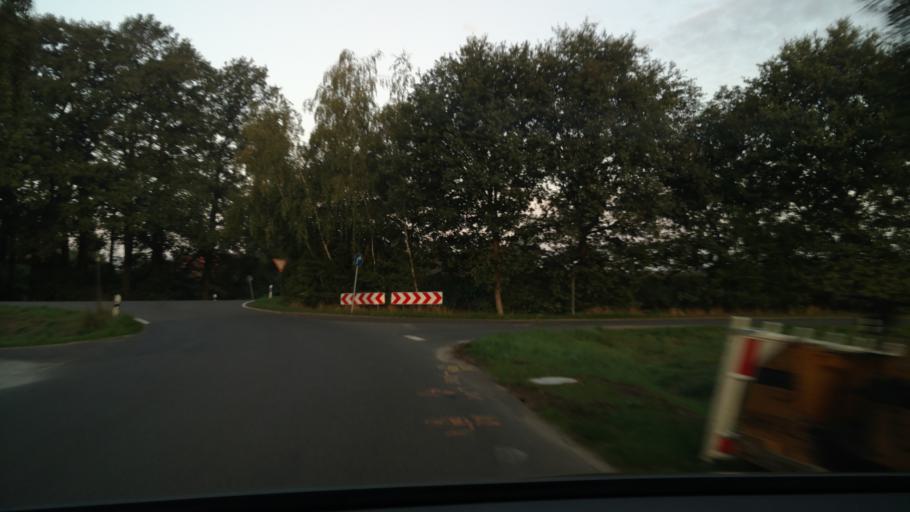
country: DE
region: North Rhine-Westphalia
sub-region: Regierungsbezirk Munster
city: Klein Reken
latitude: 51.8547
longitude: 7.0567
